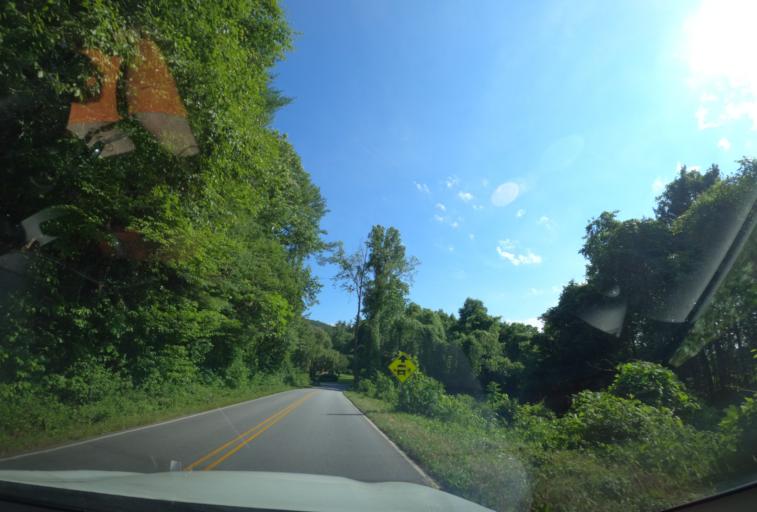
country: US
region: North Carolina
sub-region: Transylvania County
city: Brevard
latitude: 35.2567
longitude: -82.6698
